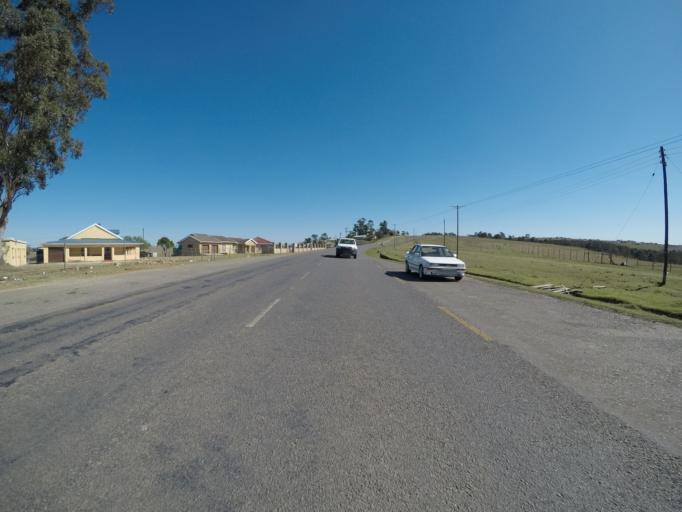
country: ZA
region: Eastern Cape
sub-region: OR Tambo District Municipality
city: Mthatha
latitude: -31.7970
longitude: 28.7451
